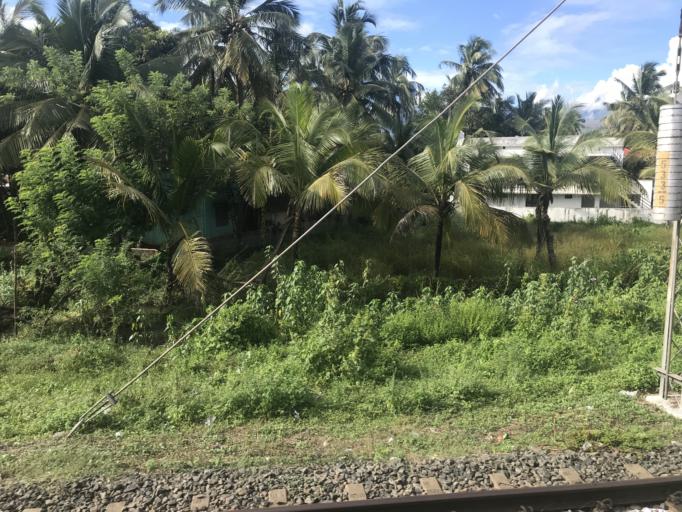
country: IN
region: Kerala
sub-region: Palakkad district
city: Palakkad
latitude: 10.8052
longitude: 76.6483
